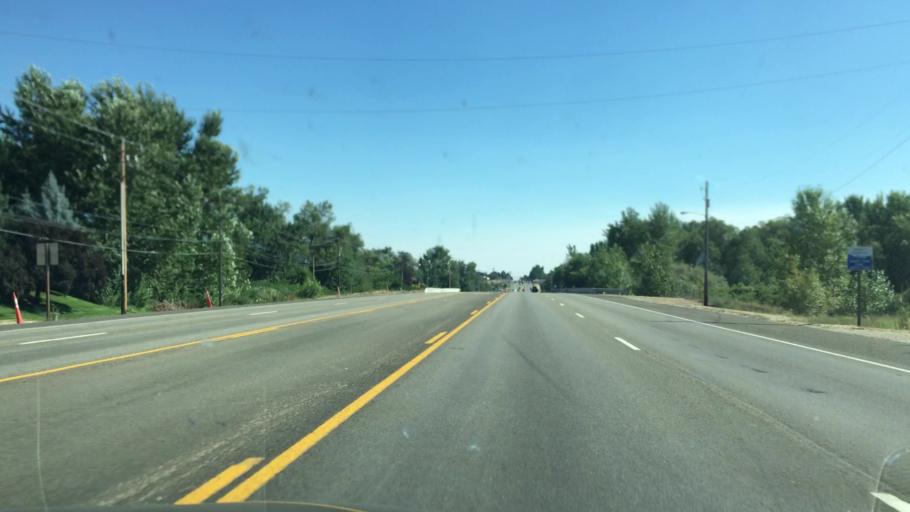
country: US
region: Idaho
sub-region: Ada County
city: Eagle
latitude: 43.6770
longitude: -116.3542
